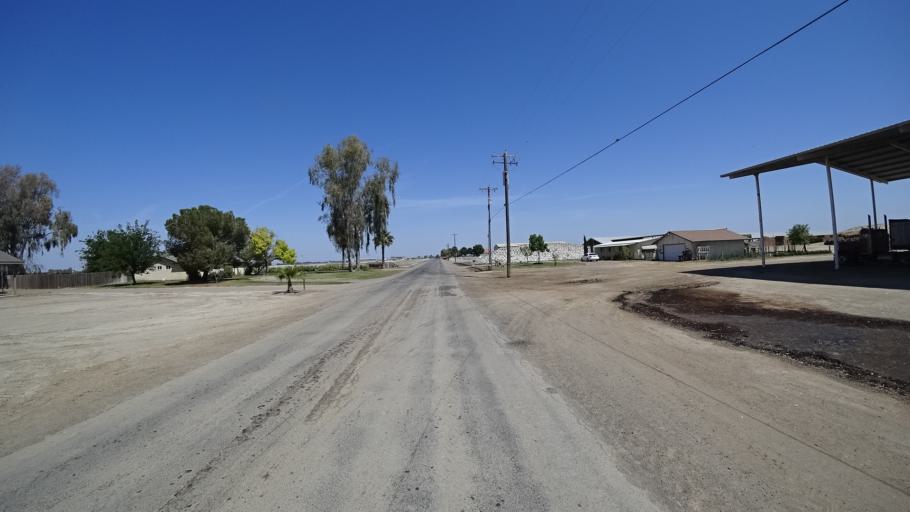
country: US
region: California
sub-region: Kings County
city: Stratford
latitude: 36.2074
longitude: -119.7623
